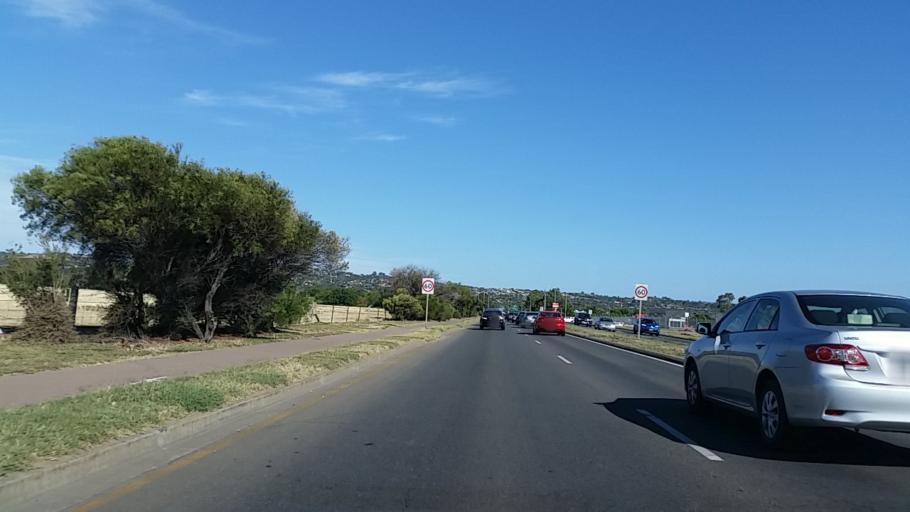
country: AU
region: South Australia
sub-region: Salisbury
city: Salisbury
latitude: -34.7884
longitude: 138.6416
